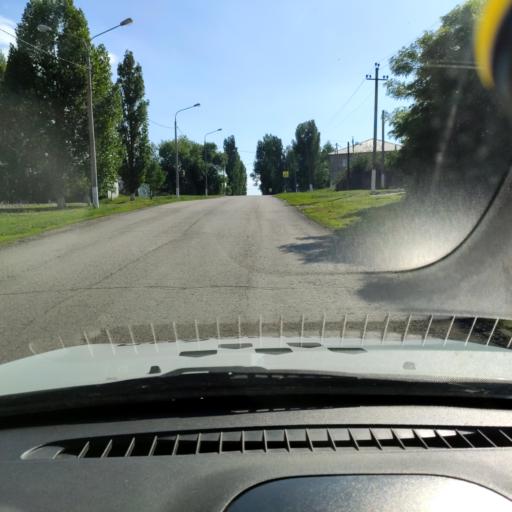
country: RU
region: Samara
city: Tol'yatti
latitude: 53.3541
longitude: 49.3025
